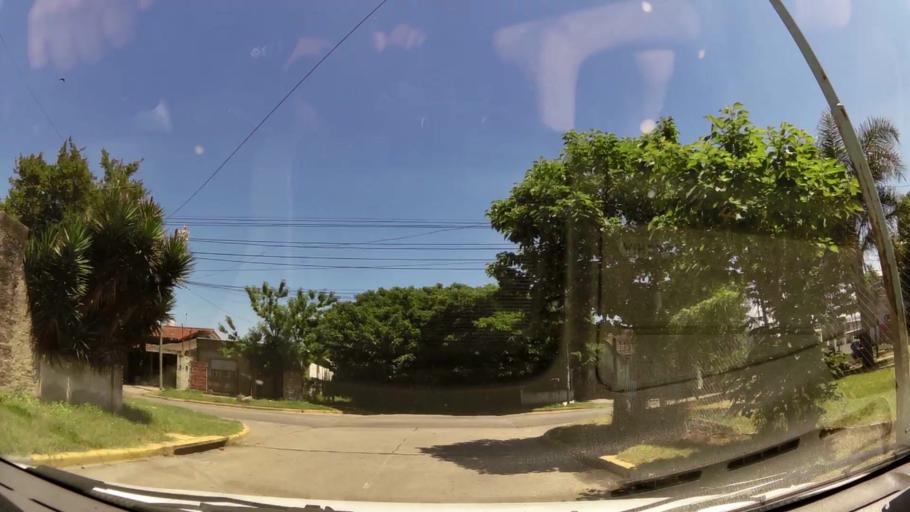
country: AR
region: Buenos Aires
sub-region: Partido de Merlo
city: Merlo
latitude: -34.6578
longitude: -58.7126
